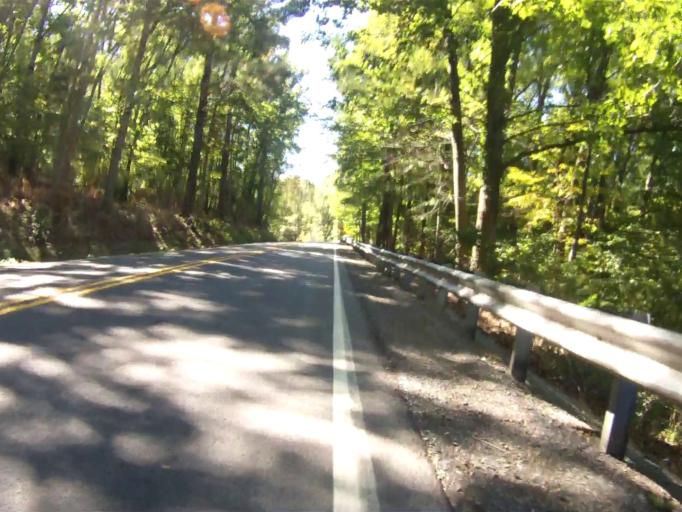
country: US
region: Pennsylvania
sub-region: Centre County
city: Park Forest Village
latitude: 40.9272
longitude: -77.9200
